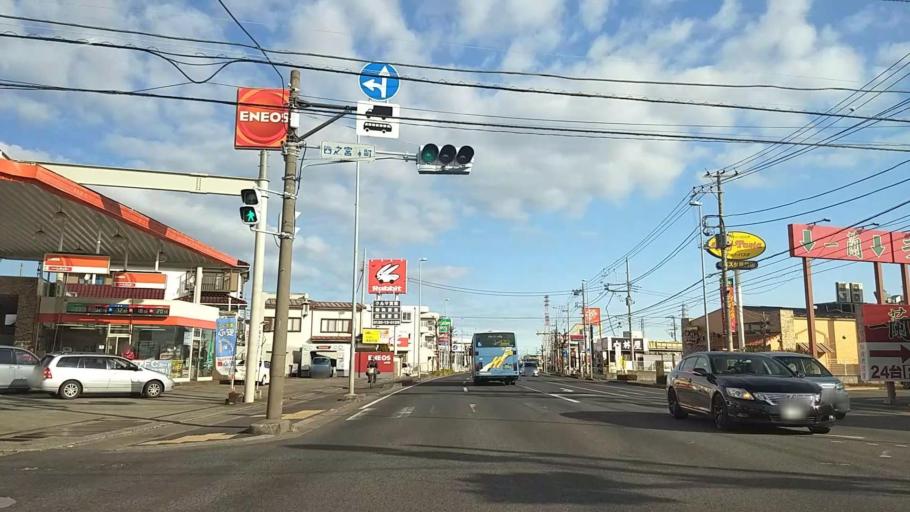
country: JP
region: Kanagawa
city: Hiratsuka
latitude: 35.3594
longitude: 139.3586
